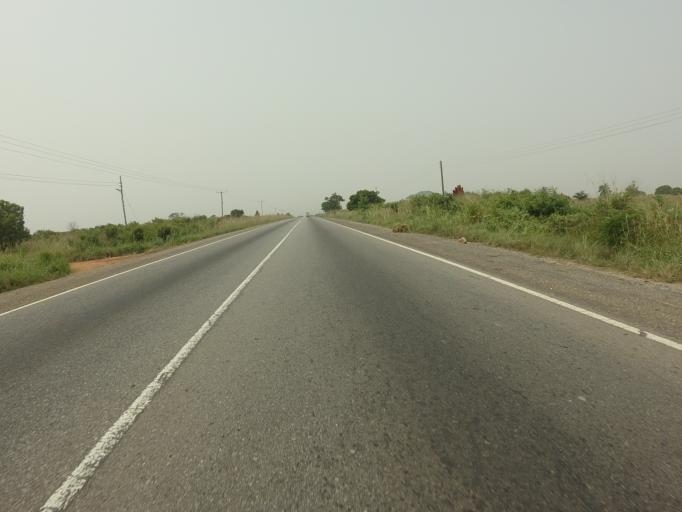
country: GH
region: Volta
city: Anloga
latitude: 5.8898
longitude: 0.4713
